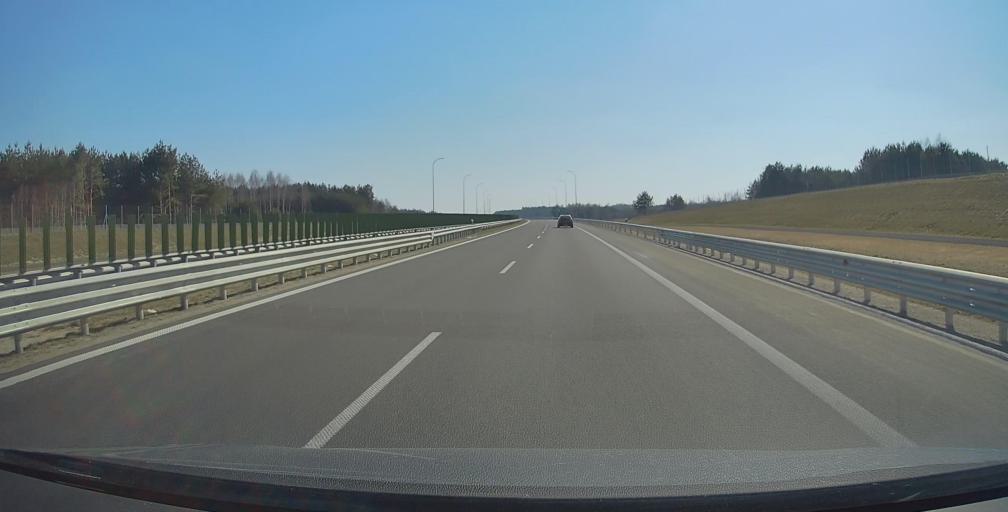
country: PL
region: Subcarpathian Voivodeship
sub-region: Powiat nizanski
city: Jezowe
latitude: 50.3933
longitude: 22.1461
